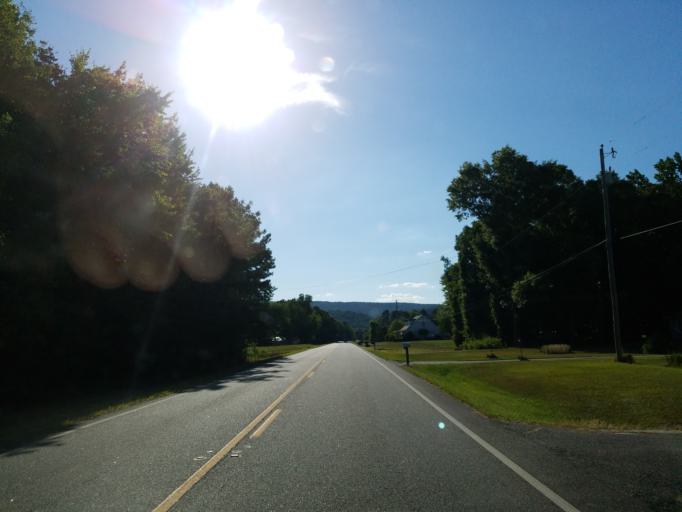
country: US
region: Georgia
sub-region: Gordon County
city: Calhoun
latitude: 34.5949
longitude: -85.0270
